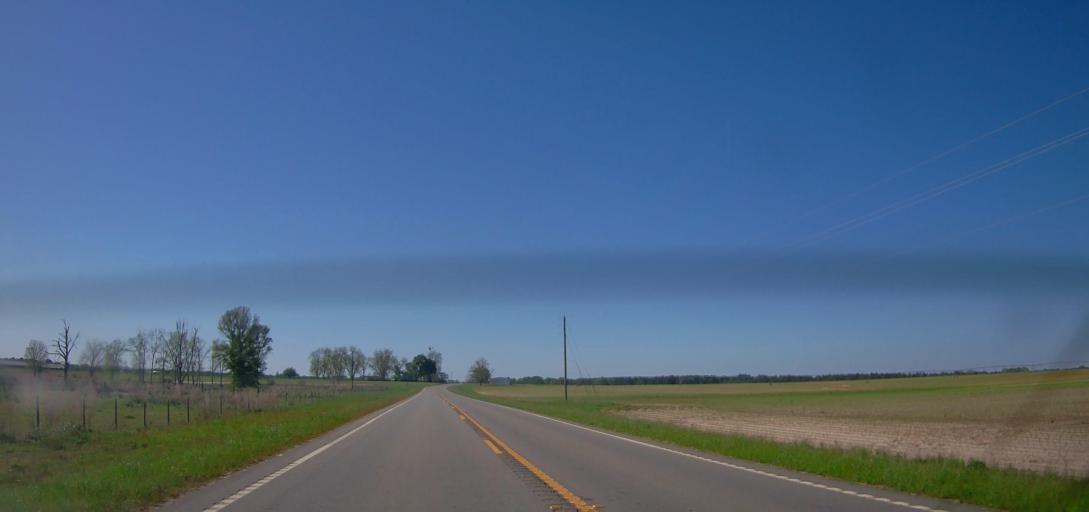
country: US
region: Georgia
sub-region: Pulaski County
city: Hawkinsville
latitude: 32.1415
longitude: -83.5098
